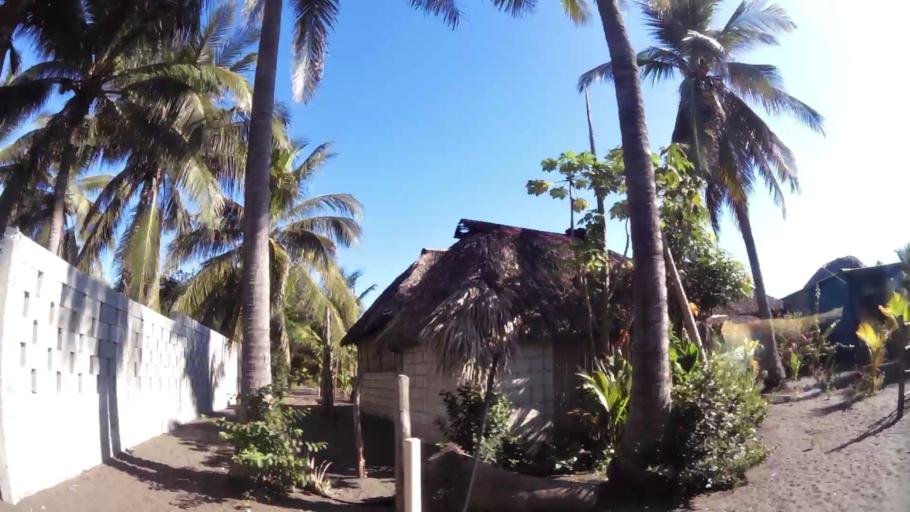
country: GT
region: Santa Rosa
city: Guazacapan
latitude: 13.8619
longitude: -90.4019
